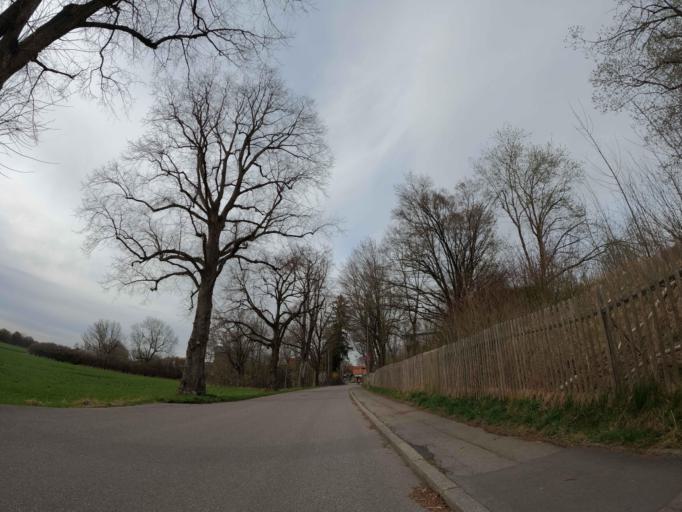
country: DE
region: Bavaria
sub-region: Upper Bavaria
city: Taufkirchen
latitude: 48.0463
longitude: 11.6240
